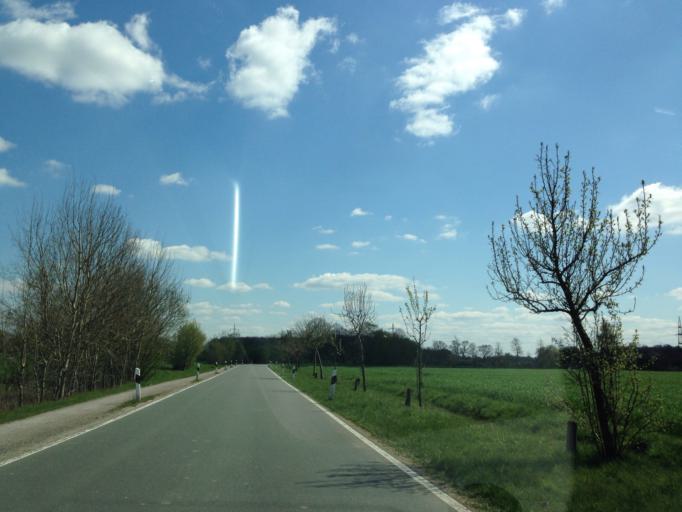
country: DE
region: North Rhine-Westphalia
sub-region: Regierungsbezirk Munster
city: Muenster
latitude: 51.9849
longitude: 7.5710
